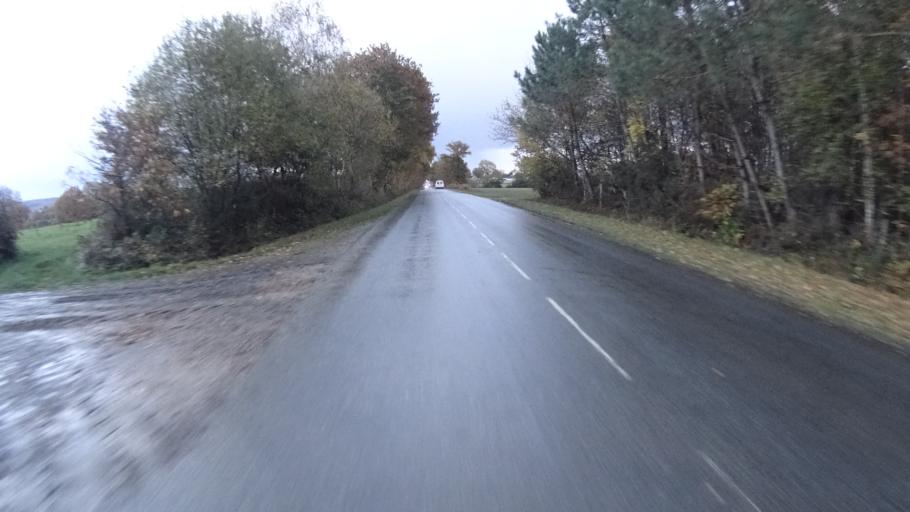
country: FR
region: Brittany
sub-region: Departement d'Ille-et-Vilaine
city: Sainte-Marie
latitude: 47.6979
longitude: -2.0161
